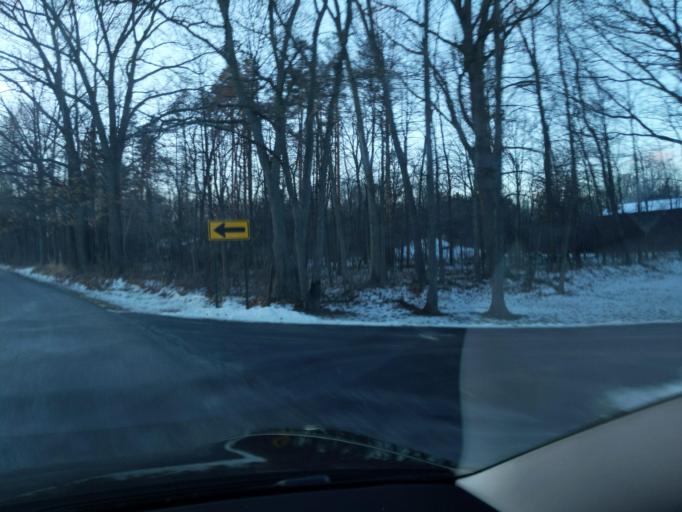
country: US
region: Michigan
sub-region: Ingham County
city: Stockbridge
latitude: 42.4717
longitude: -84.2924
